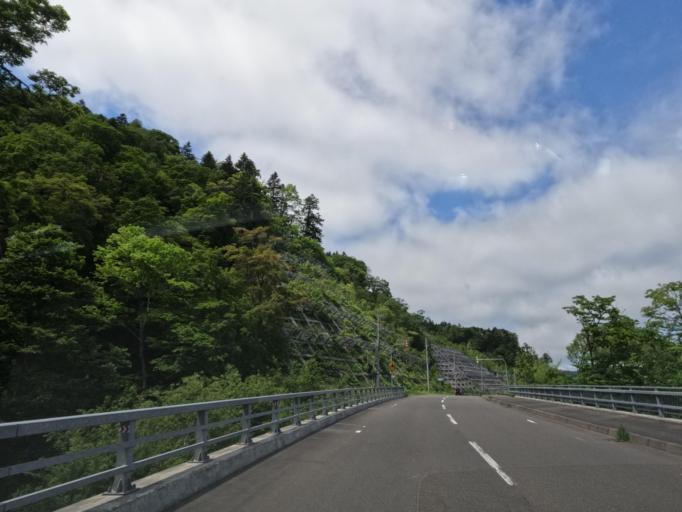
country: JP
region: Hokkaido
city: Tobetsu
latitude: 43.3325
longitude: 141.5687
